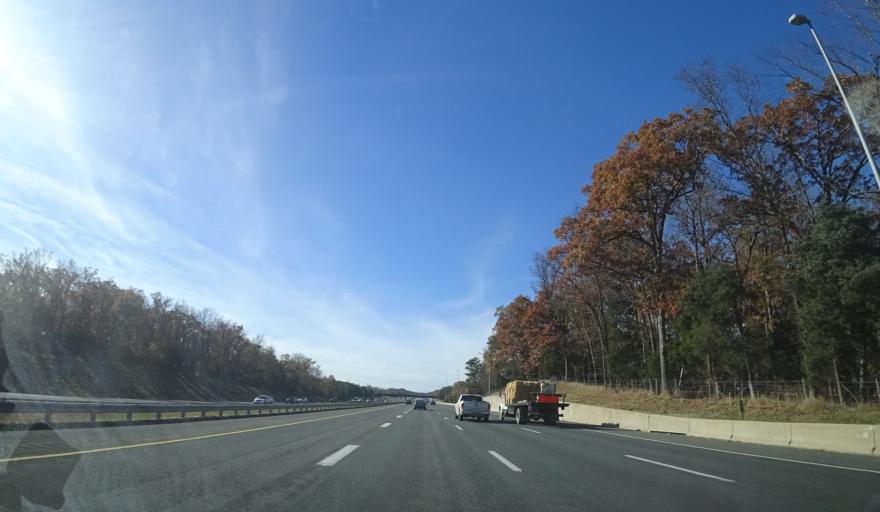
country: US
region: Virginia
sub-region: Prince William County
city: Bull Run
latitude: 38.8001
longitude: -77.5426
